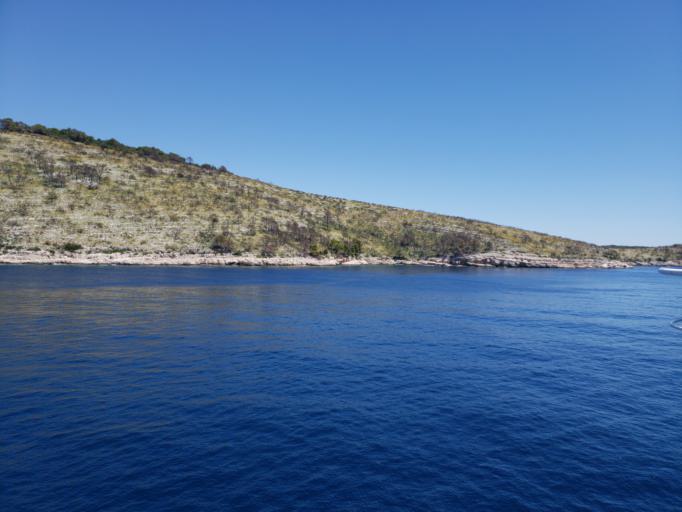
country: HR
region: Splitsko-Dalmatinska
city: Stari Grad
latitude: 43.2158
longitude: 16.5259
